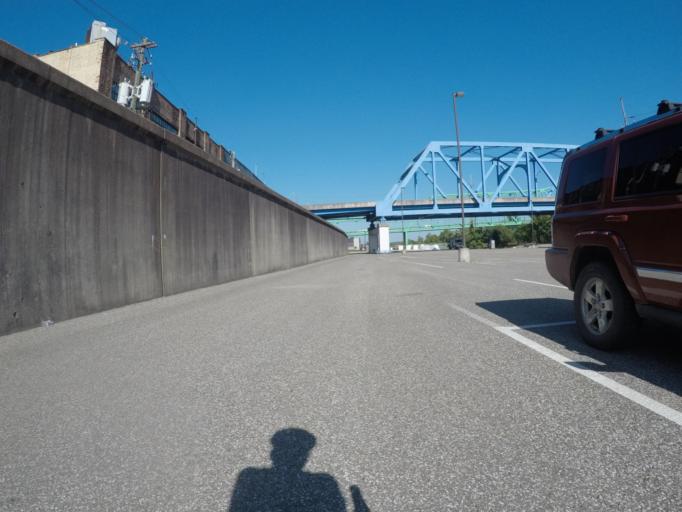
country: US
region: Kentucky
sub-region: Boyd County
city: Ashland
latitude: 38.4815
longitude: -82.6409
